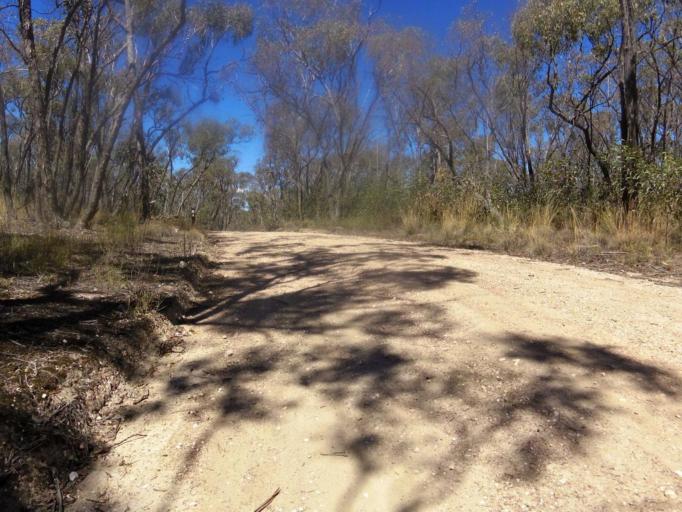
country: AU
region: Victoria
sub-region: Mount Alexander
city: Castlemaine
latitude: -37.0020
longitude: 144.1094
